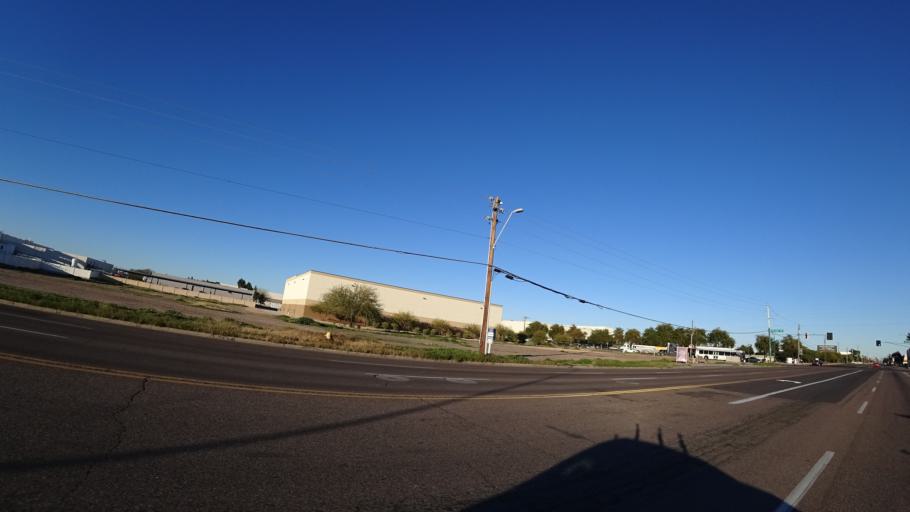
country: US
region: Arizona
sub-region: Maricopa County
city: Laveen
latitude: 33.4512
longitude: -112.1704
